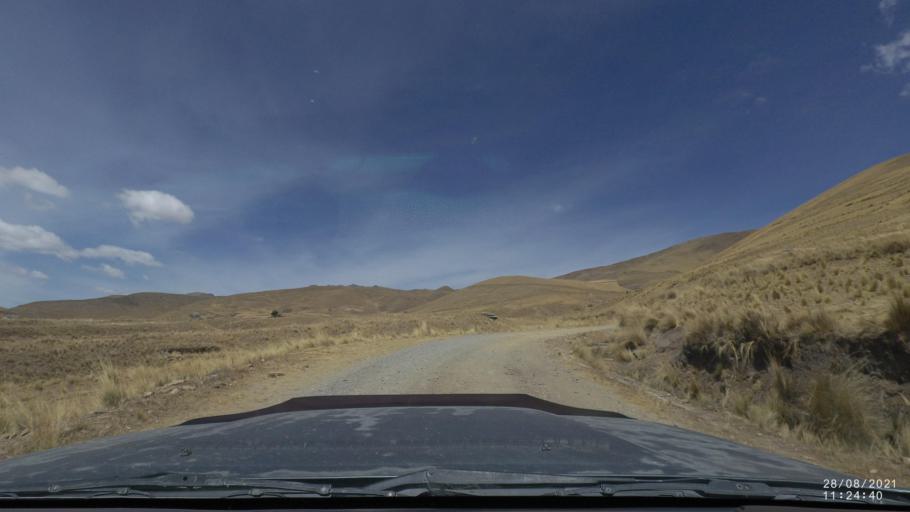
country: BO
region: Cochabamba
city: Sipe Sipe
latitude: -17.1683
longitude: -66.3511
